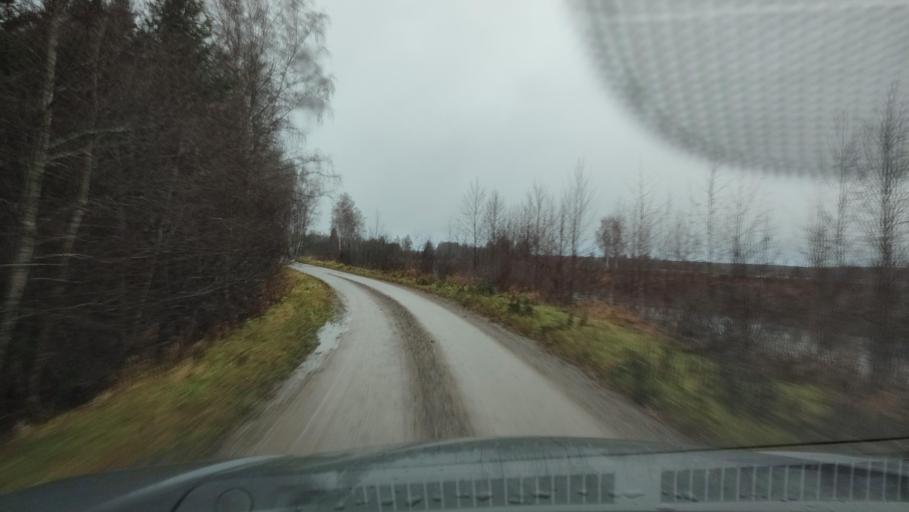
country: FI
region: Ostrobothnia
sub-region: Sydosterbotten
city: Kristinestad
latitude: 62.2385
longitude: 21.4674
